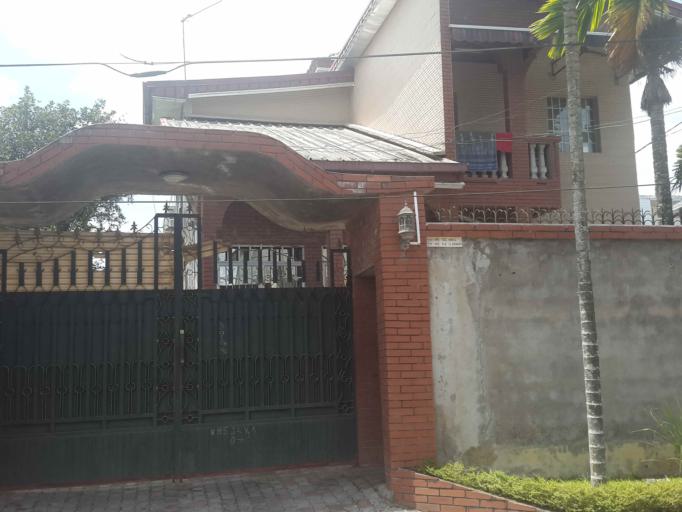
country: CM
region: Littoral
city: Douala
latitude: 4.0936
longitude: 9.7338
